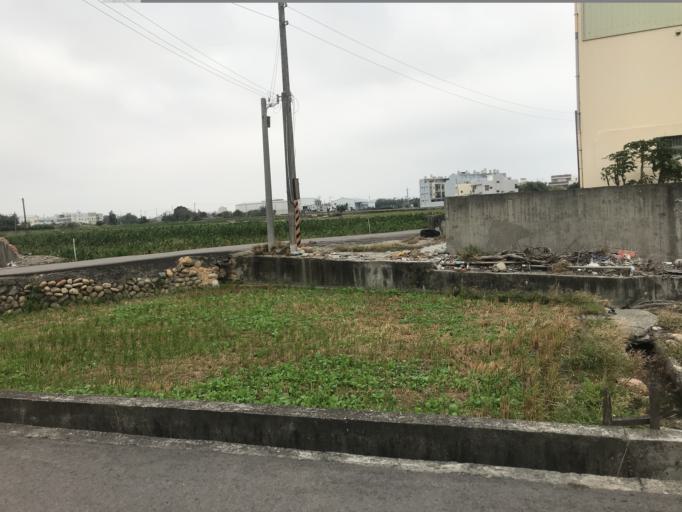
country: TW
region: Taiwan
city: Fengyuan
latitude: 24.3637
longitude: 120.6027
